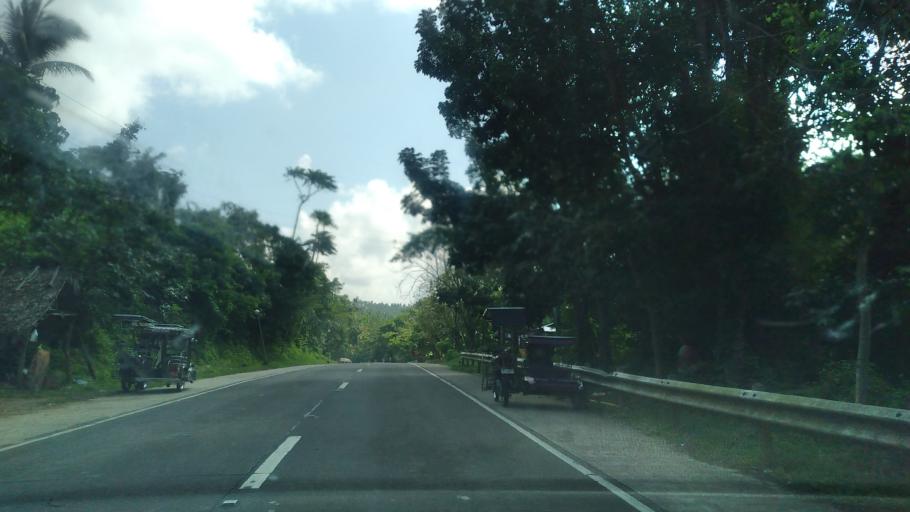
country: PH
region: Calabarzon
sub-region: Province of Quezon
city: Unisan
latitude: 13.8343
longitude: 122.0095
